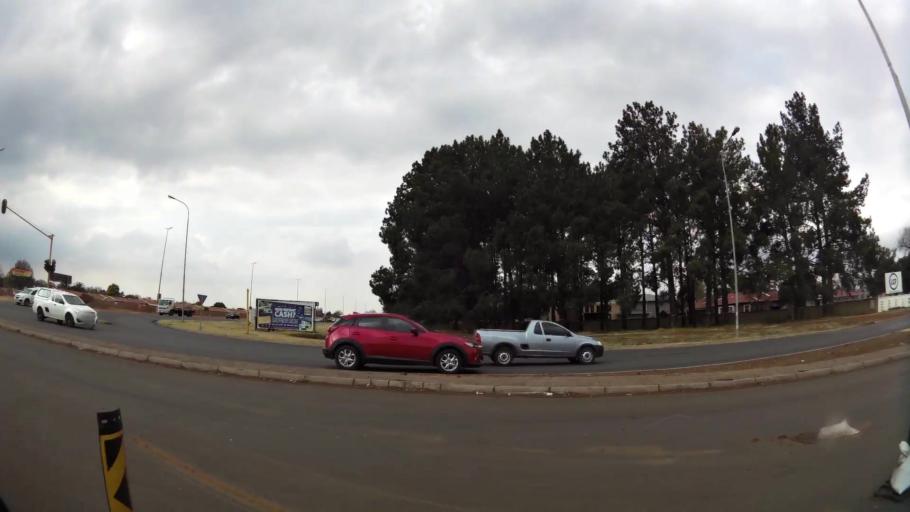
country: ZA
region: Gauteng
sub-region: Sedibeng District Municipality
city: Vanderbijlpark
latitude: -26.7078
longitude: 27.8246
